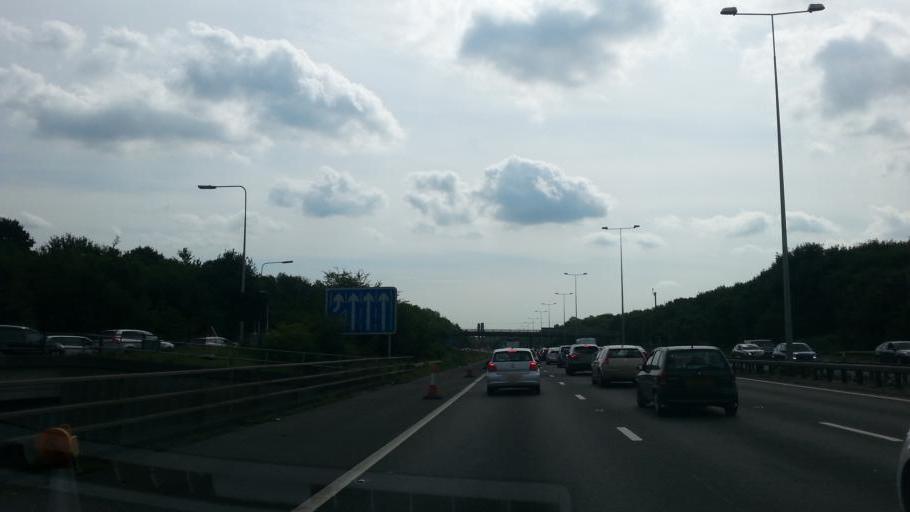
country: GB
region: England
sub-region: Surrey
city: Virginia Water
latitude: 51.3993
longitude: -0.5365
